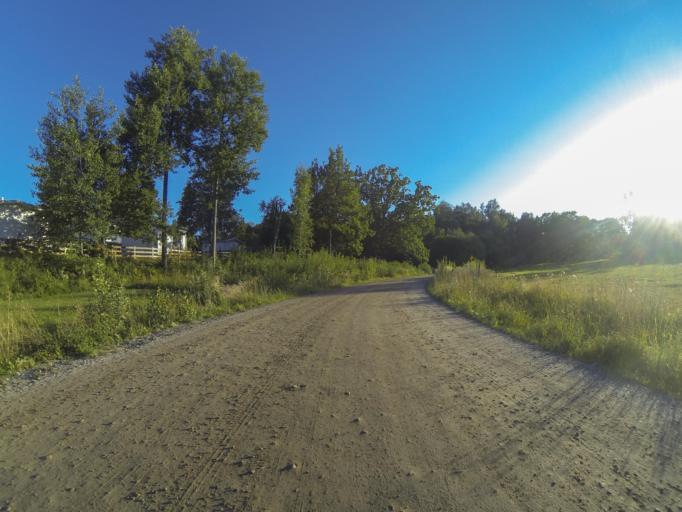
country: SE
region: Vaestmanland
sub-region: Vasteras
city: Vasteras
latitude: 59.5515
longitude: 16.6650
